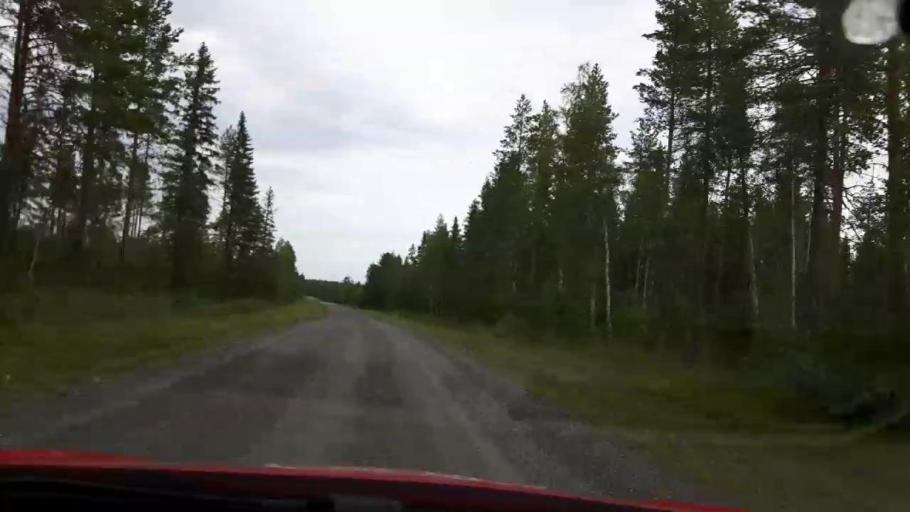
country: SE
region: Jaemtland
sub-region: Stroemsunds Kommun
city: Stroemsund
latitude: 63.7470
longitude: 15.5869
